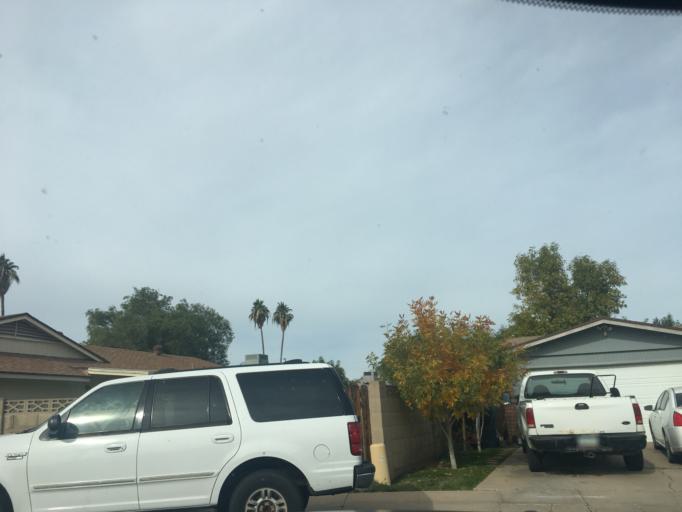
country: US
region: Arizona
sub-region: Maricopa County
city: Gilbert
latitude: 33.3488
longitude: -111.7970
